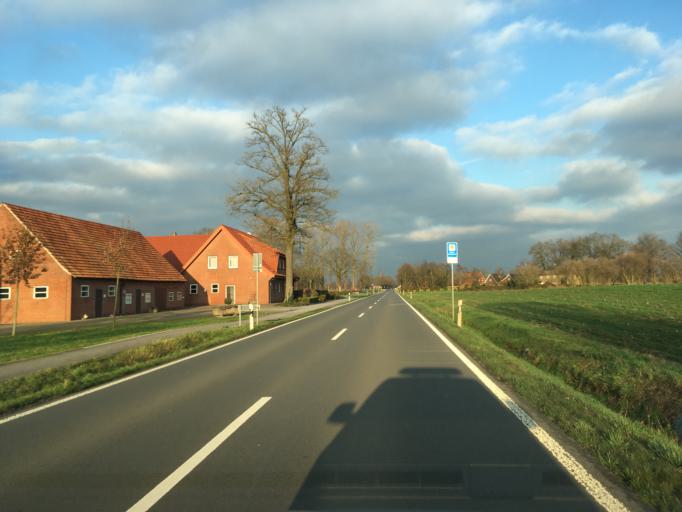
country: DE
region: North Rhine-Westphalia
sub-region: Regierungsbezirk Munster
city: Gronau
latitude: 52.1496
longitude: 7.0167
